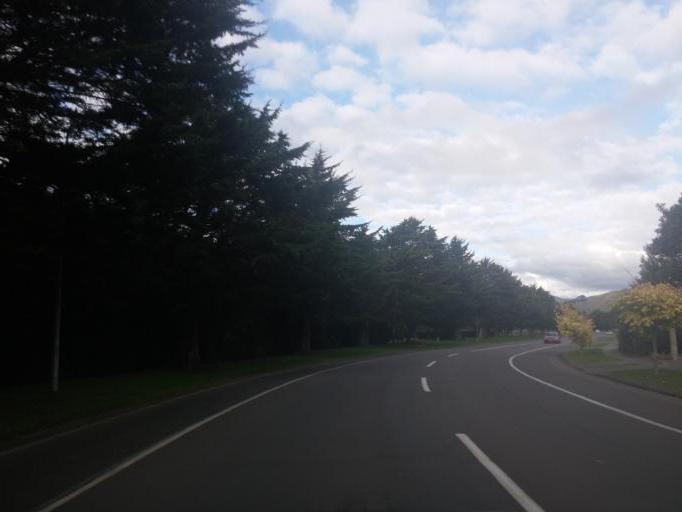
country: NZ
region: Wellington
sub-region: Kapiti Coast District
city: Paraparaumu
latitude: -40.8713
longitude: 175.0440
